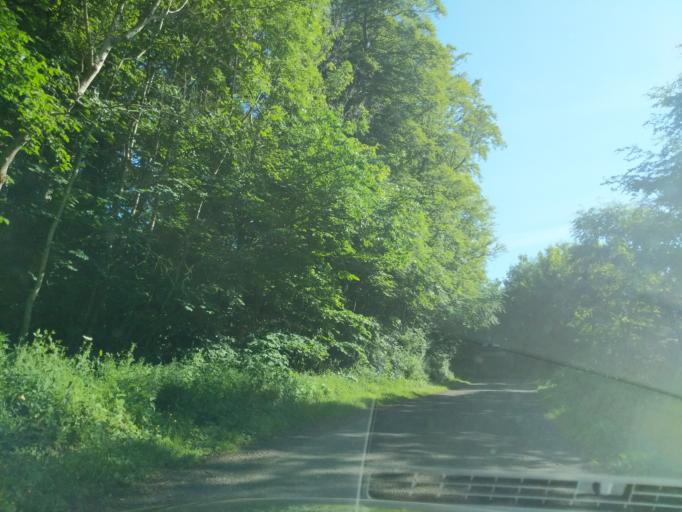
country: GB
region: Scotland
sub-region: Fife
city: Pathhead
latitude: 55.8726
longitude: -2.9707
